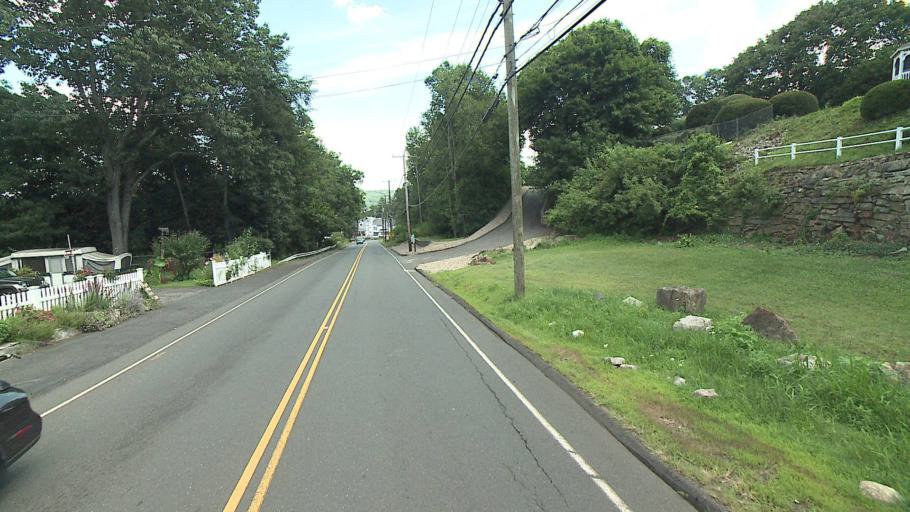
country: US
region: Connecticut
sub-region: Fairfield County
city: Shelton
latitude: 41.3192
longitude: -73.1023
